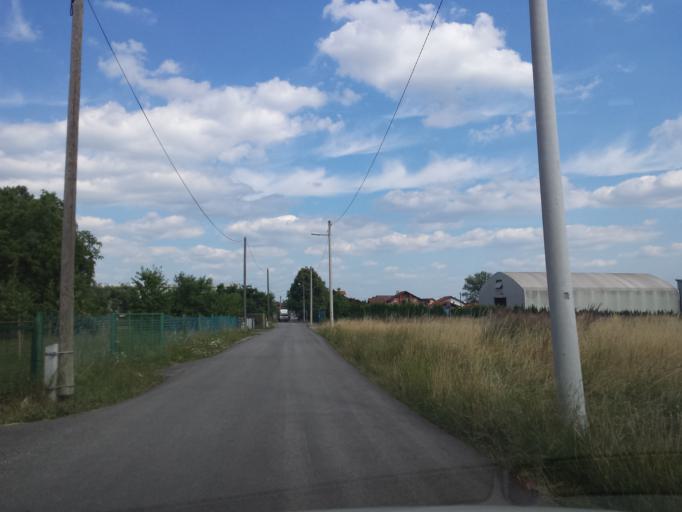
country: HR
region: Grad Zagreb
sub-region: Sesvete
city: Sesvete
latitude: 45.8238
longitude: 16.1483
